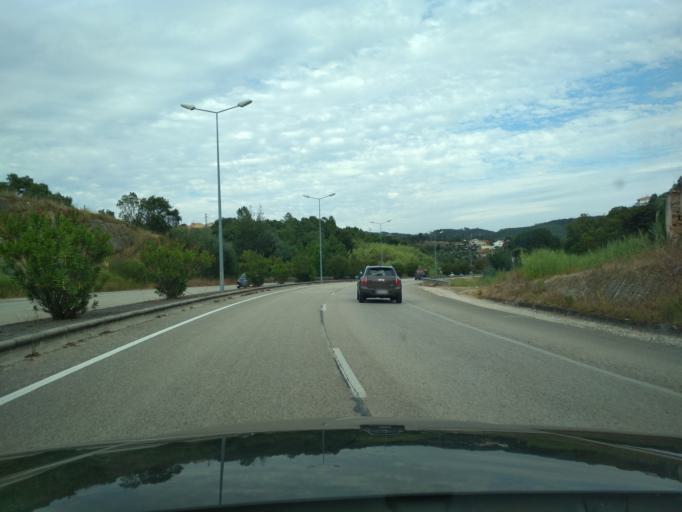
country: PT
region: Coimbra
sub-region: Coimbra
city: Coimbra
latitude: 40.2264
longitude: -8.4152
